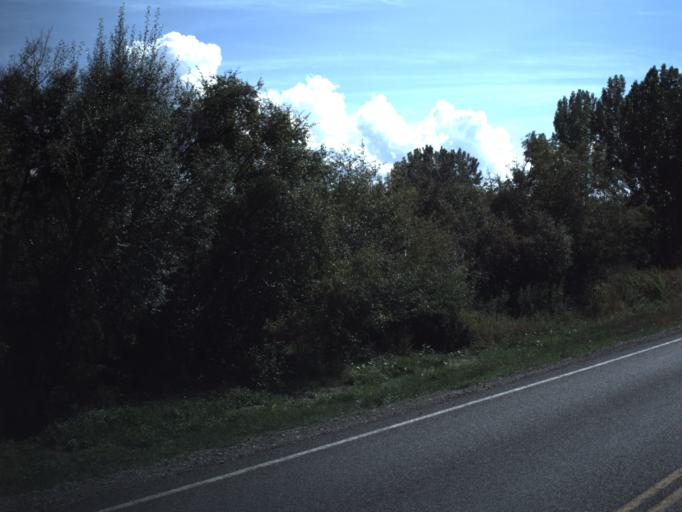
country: US
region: Idaho
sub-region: Bear Lake County
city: Paris
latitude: 41.9233
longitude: -111.3968
